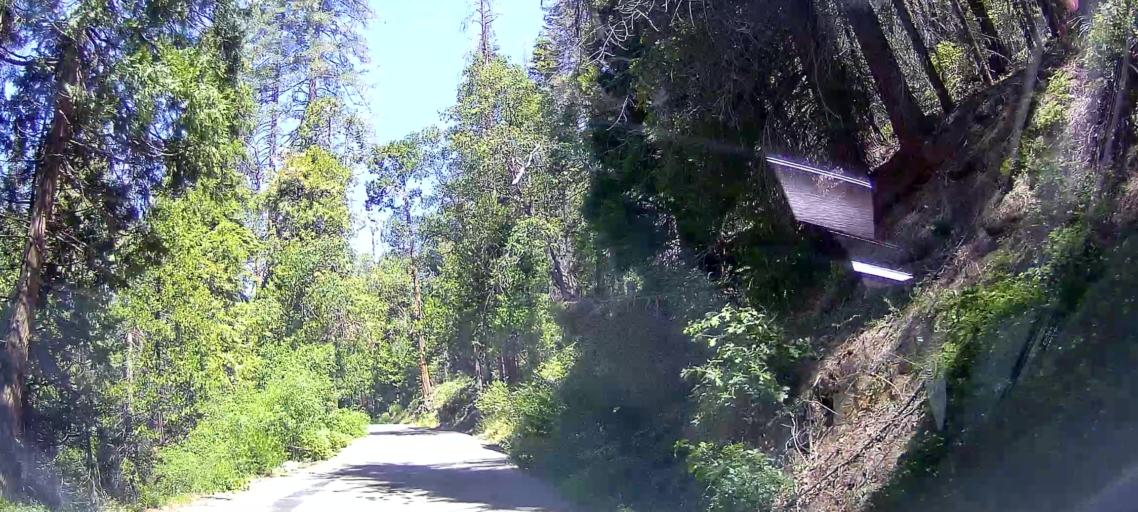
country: US
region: California
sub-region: Tulare County
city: Three Rivers
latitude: 36.5603
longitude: -118.7840
